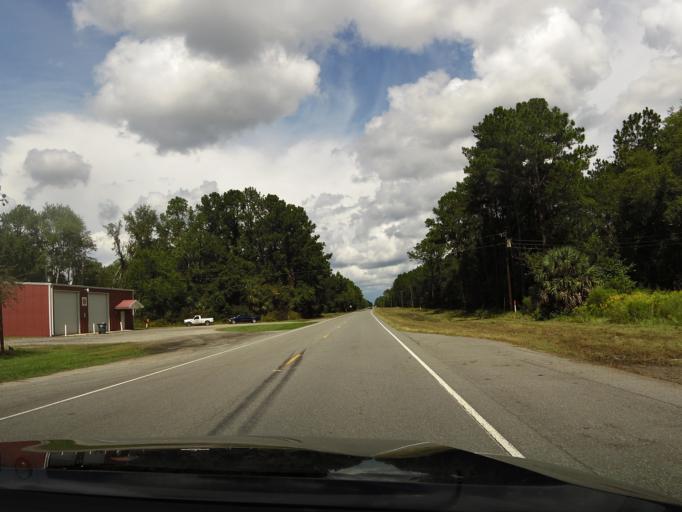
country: US
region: Georgia
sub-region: Brantley County
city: Nahunta
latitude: 31.0398
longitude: -82.0198
